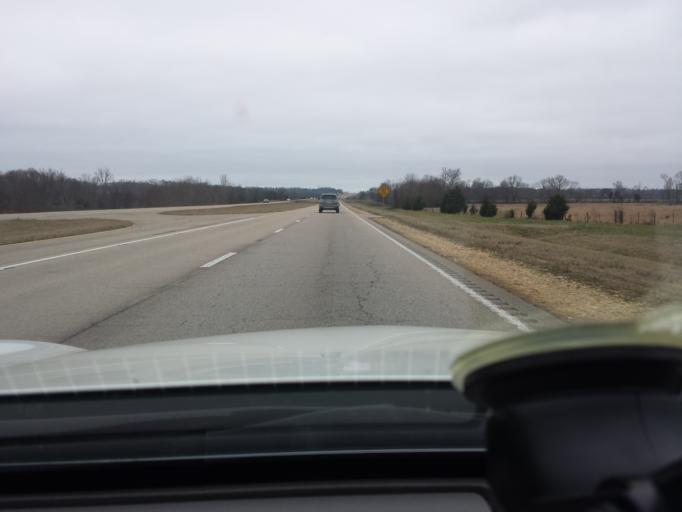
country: US
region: Mississippi
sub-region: Lee County
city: Shannon
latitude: 34.0637
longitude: -88.7035
